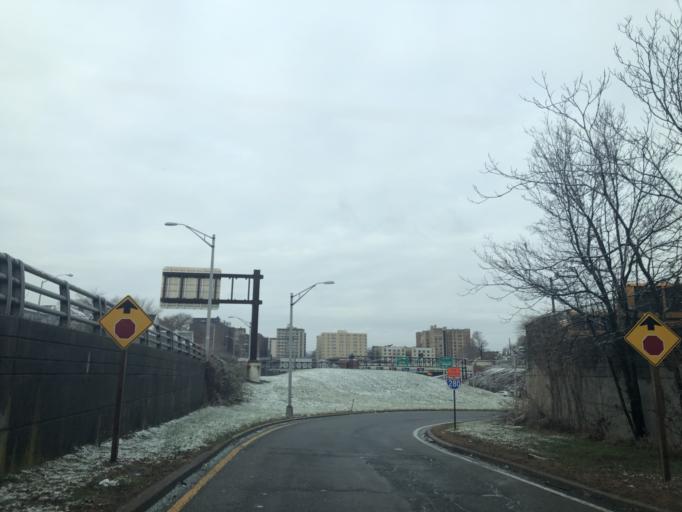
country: US
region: New Jersey
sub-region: Essex County
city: East Orange
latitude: 40.7547
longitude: -74.2053
